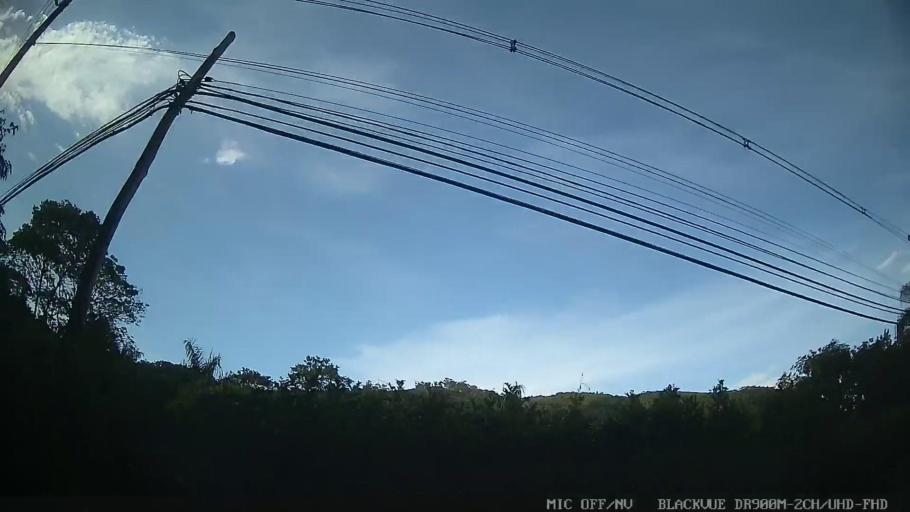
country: BR
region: Sao Paulo
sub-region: Serra Negra
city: Serra Negra
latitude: -22.7000
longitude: -46.6477
